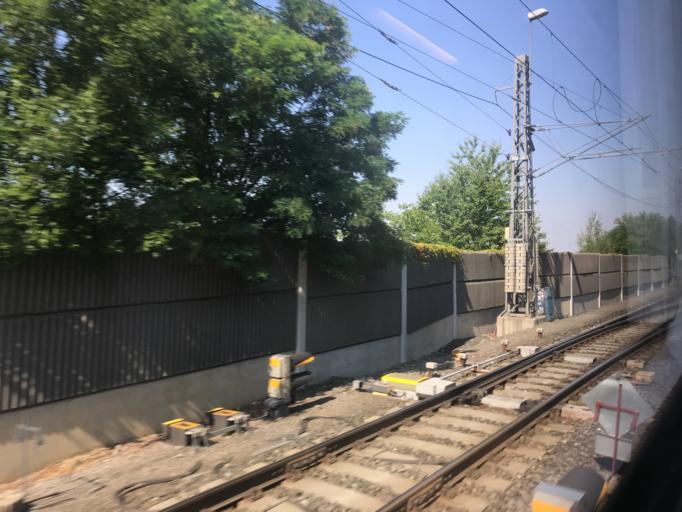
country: CZ
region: Central Bohemia
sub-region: Okres Praha-Vychod
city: Ricany
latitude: 50.0007
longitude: 14.6566
